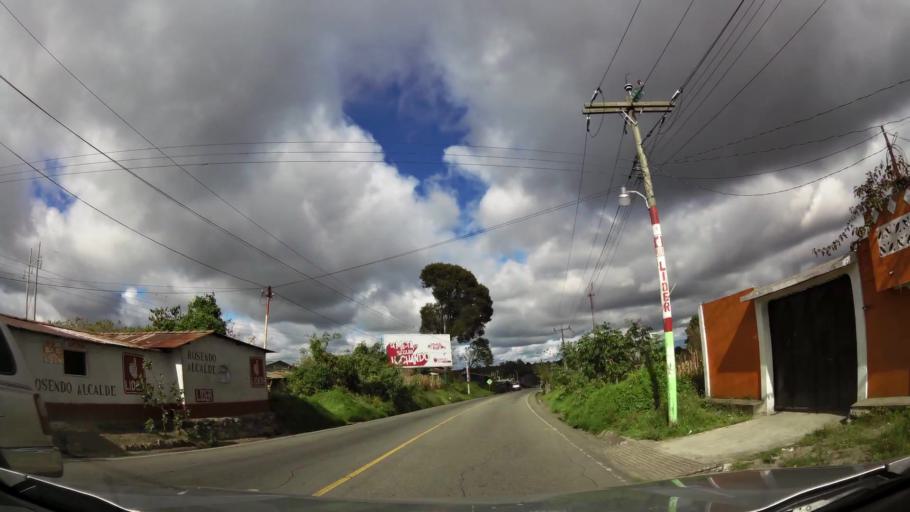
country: GT
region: Quiche
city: Chichicastenango
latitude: 14.8723
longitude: -91.1416
